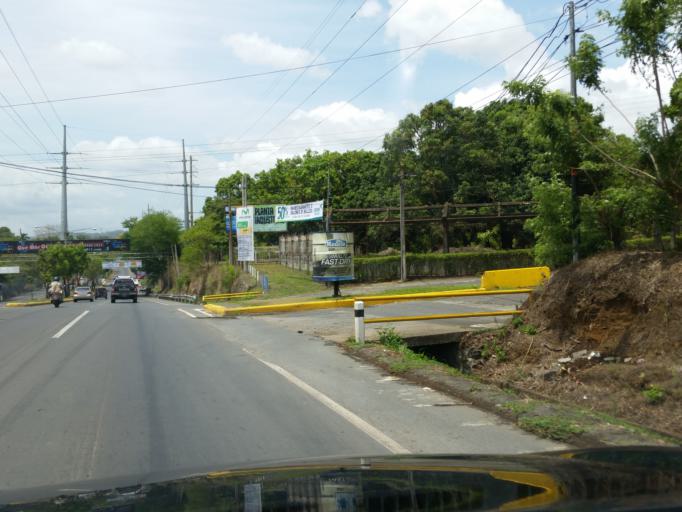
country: NI
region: Masaya
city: Ticuantepe
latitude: 12.0601
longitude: -86.2071
